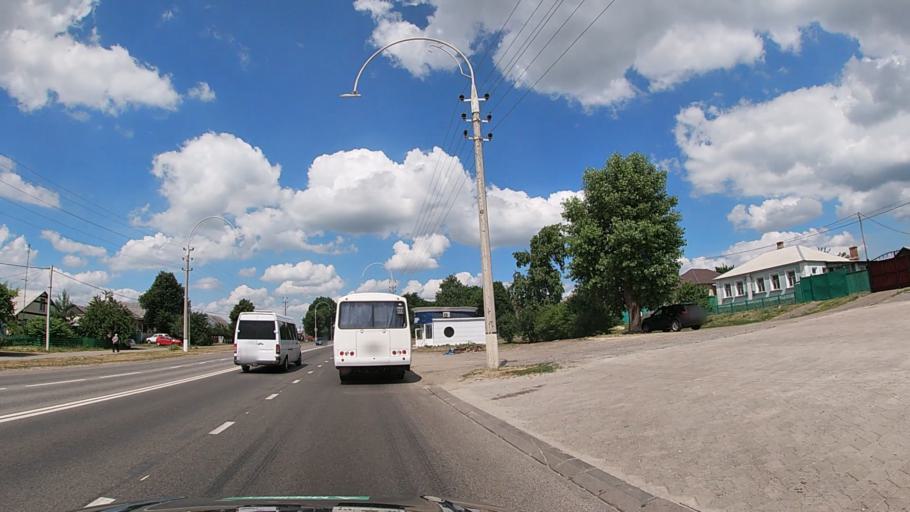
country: RU
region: Belgorod
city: Severnyy
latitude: 50.6255
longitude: 36.4984
